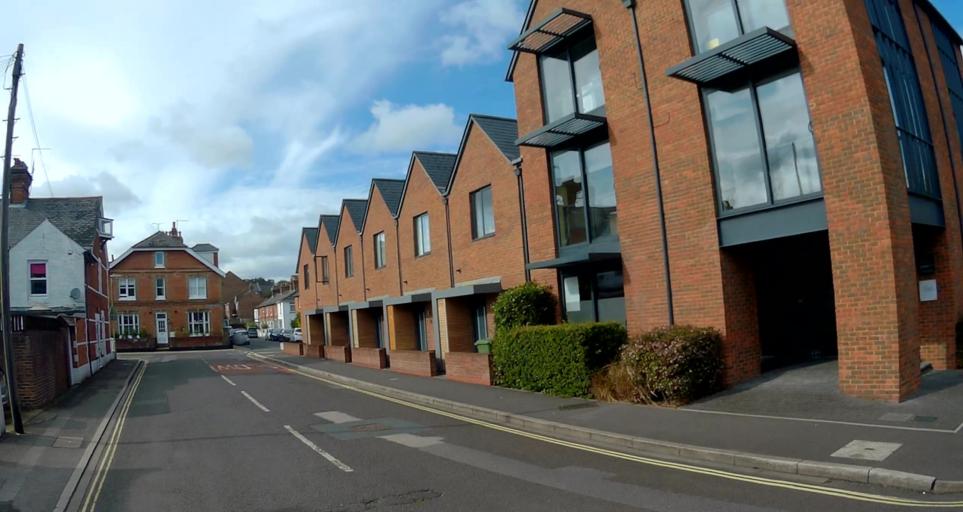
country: GB
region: England
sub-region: Hampshire
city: Winchester
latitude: 51.0661
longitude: -1.3125
